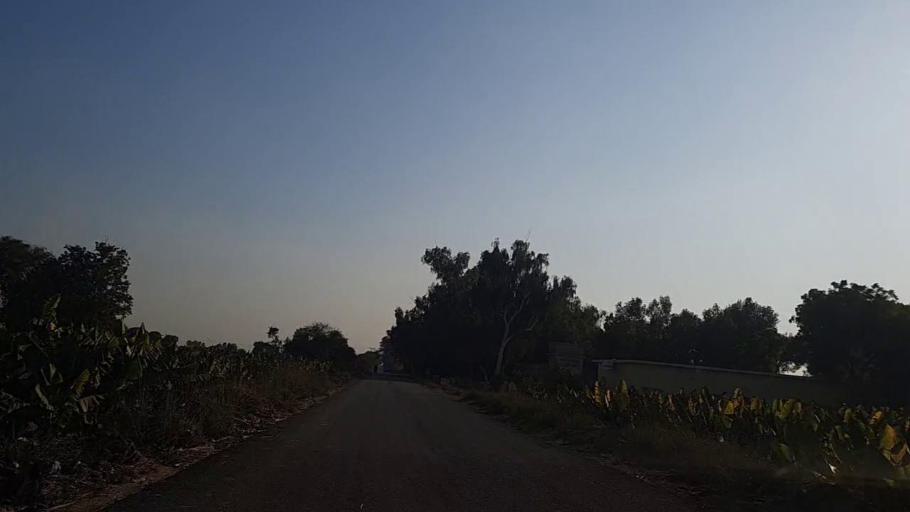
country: PK
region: Sindh
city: Daur
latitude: 26.3319
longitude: 68.1463
